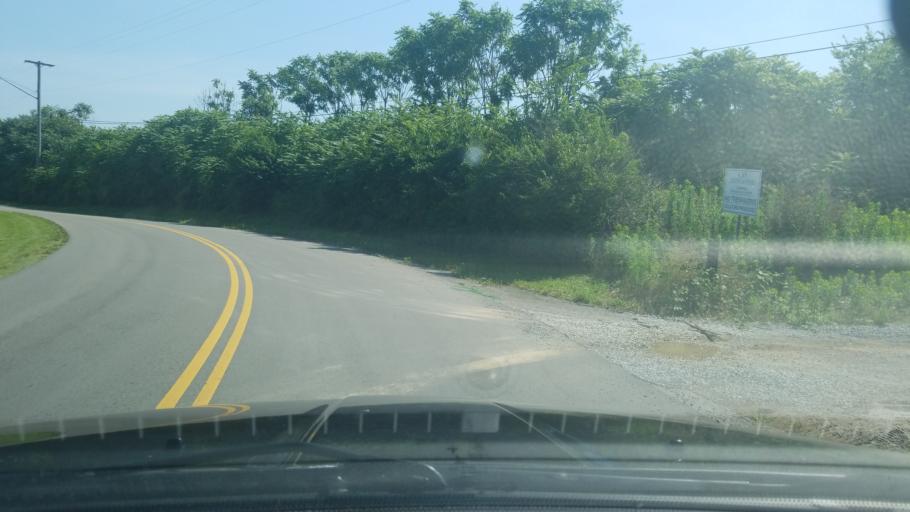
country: US
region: Tennessee
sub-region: Davidson County
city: Oak Hill
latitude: 36.1143
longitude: -86.7519
